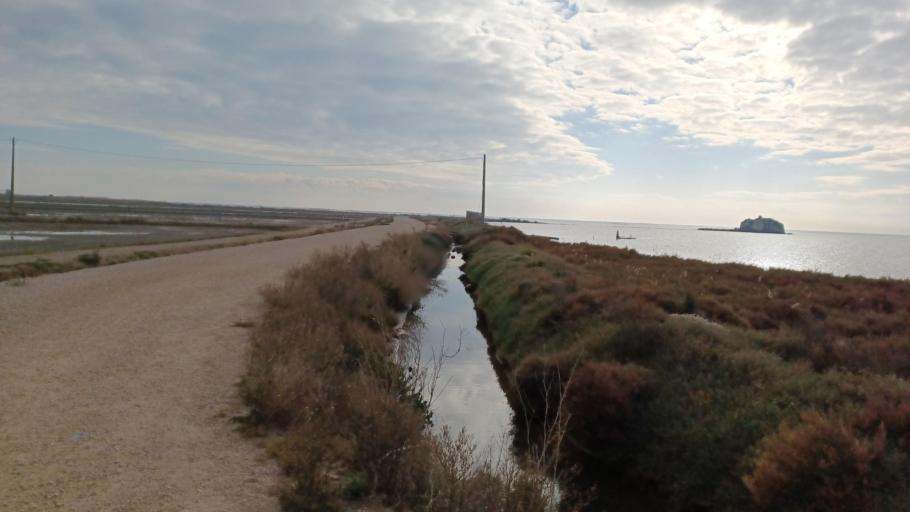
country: ES
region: Catalonia
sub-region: Provincia de Tarragona
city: Deltebre
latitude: 40.6382
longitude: 0.7047
